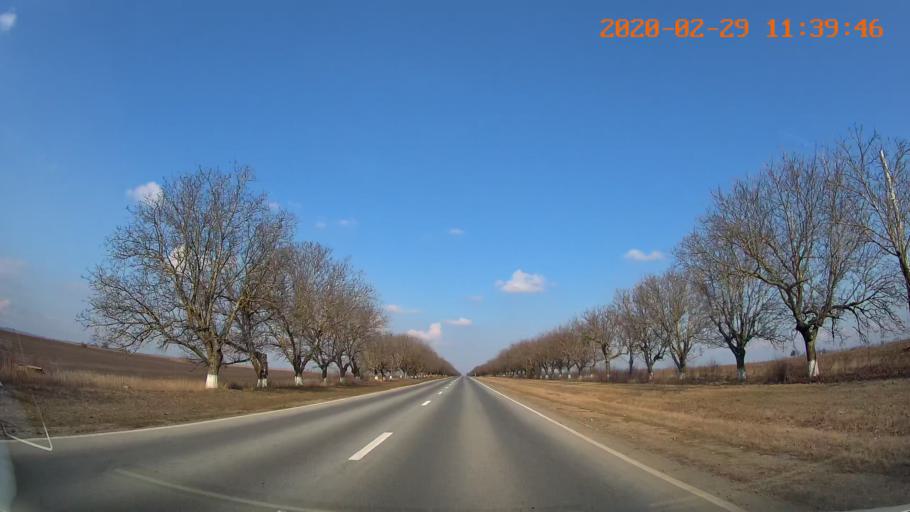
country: MD
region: Rezina
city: Saharna
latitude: 47.6452
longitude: 29.0230
